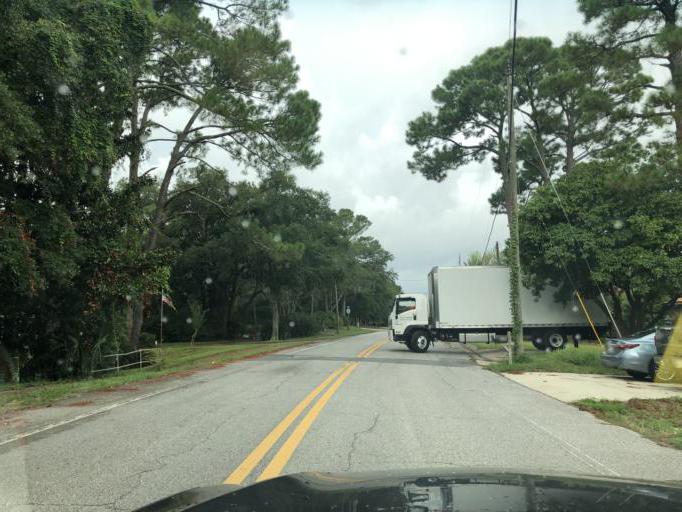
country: US
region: Florida
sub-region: Okaloosa County
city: Destin
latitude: 30.4054
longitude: -86.5006
